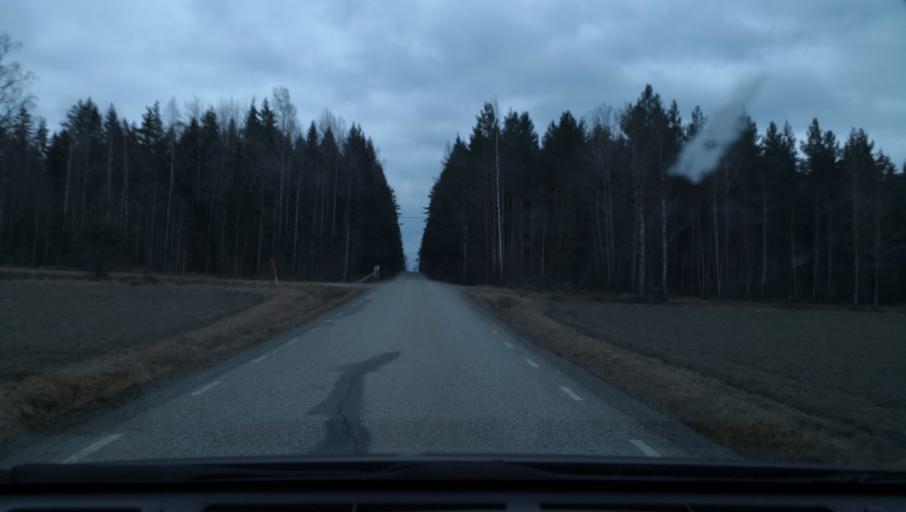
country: SE
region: OErebro
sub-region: Lindesbergs Kommun
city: Fellingsbro
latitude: 59.5559
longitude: 15.6004
